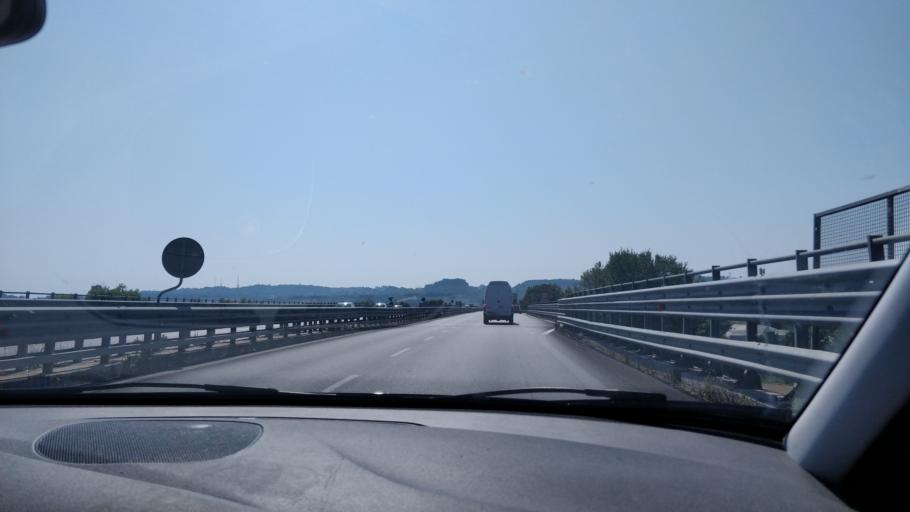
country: IT
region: Abruzzo
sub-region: Provincia di Pescara
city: Villa Raspa
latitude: 42.4470
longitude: 14.1853
